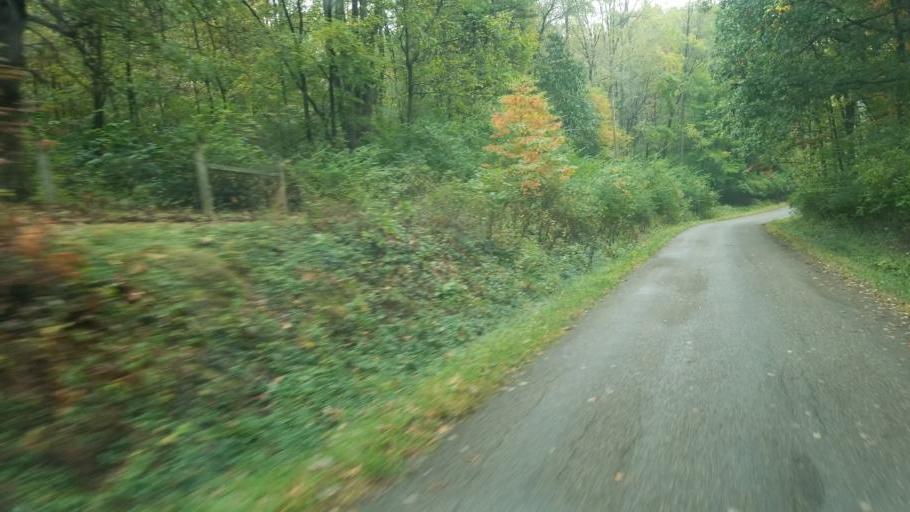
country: US
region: Ohio
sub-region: Ashland County
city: Loudonville
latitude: 40.5797
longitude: -82.2764
